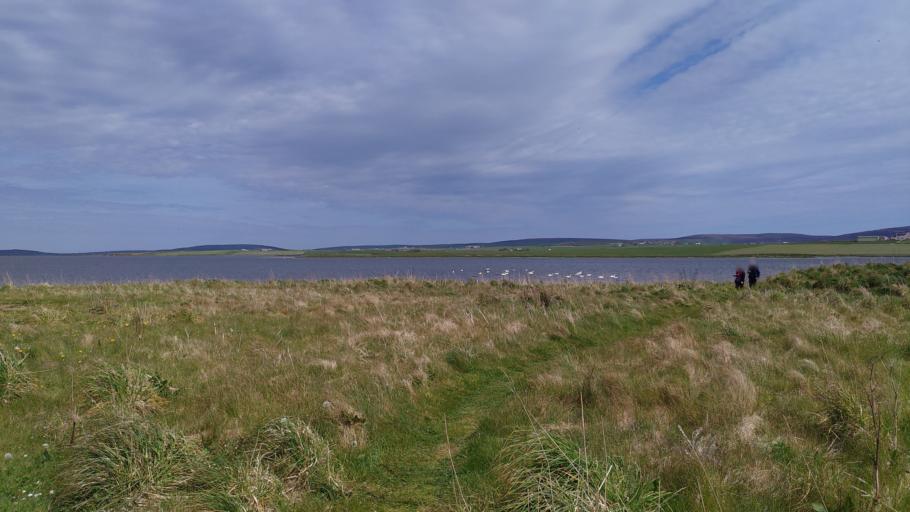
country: GB
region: Scotland
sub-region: Orkney Islands
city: Stromness
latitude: 58.9957
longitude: -3.2064
